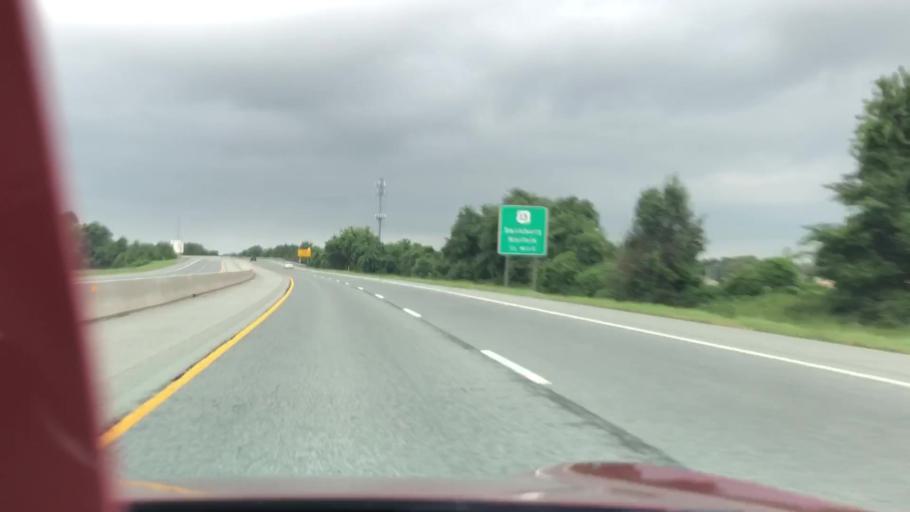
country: US
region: Delaware
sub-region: Kent County
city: Kent Acres
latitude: 39.1415
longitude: -75.5191
